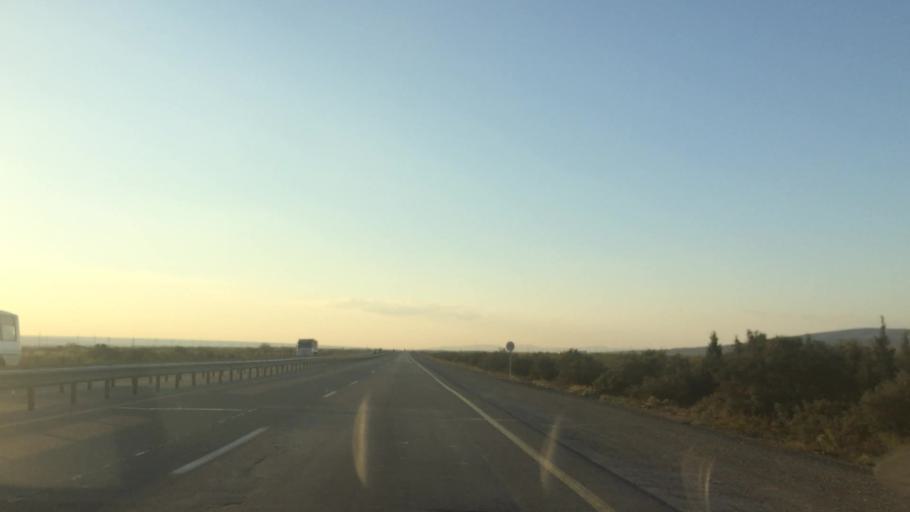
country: AZ
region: Baki
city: Qobustan
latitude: 39.9518
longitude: 49.3196
